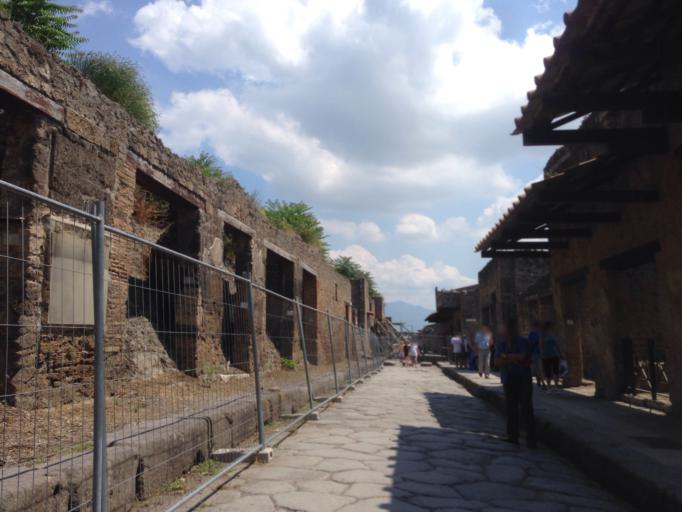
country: IT
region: Campania
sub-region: Provincia di Napoli
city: Pompei
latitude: 40.7511
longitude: 14.4906
